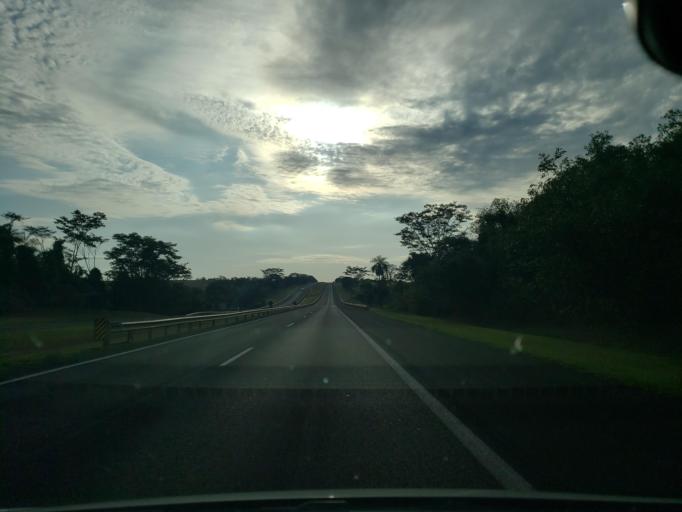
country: BR
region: Sao Paulo
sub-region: Mirandopolis
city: Mirandopolis
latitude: -21.1002
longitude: -51.0405
